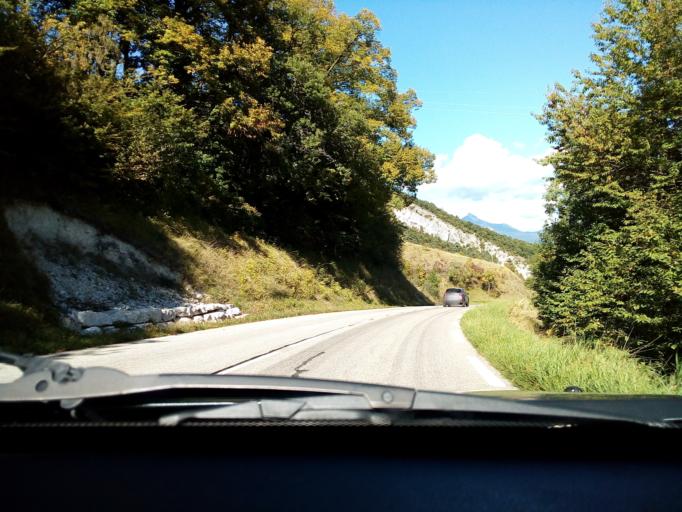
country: FR
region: Rhone-Alpes
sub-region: Departement de l'Isere
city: Sassenage
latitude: 45.2024
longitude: 5.6301
